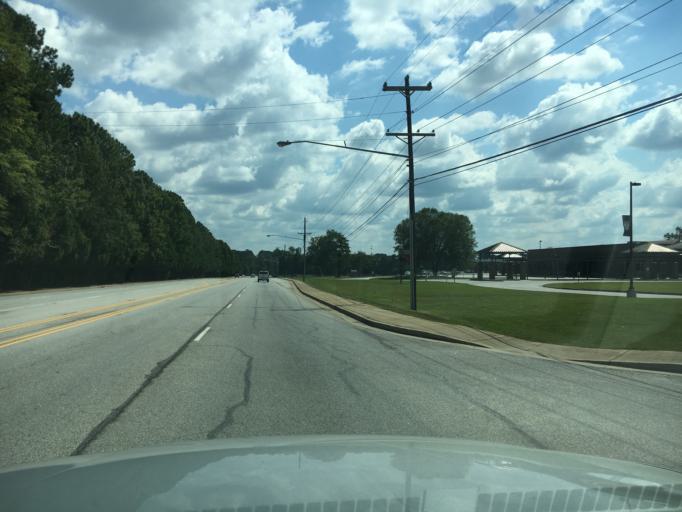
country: US
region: South Carolina
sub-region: Greenwood County
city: Greenwood
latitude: 34.1924
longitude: -82.1871
